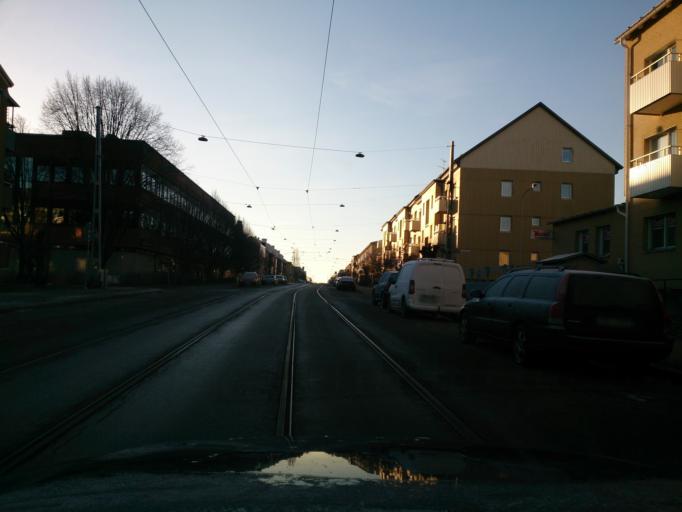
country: SE
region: OEstergoetland
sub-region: Norrkopings Kommun
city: Norrkoping
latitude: 58.6009
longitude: 16.1615
